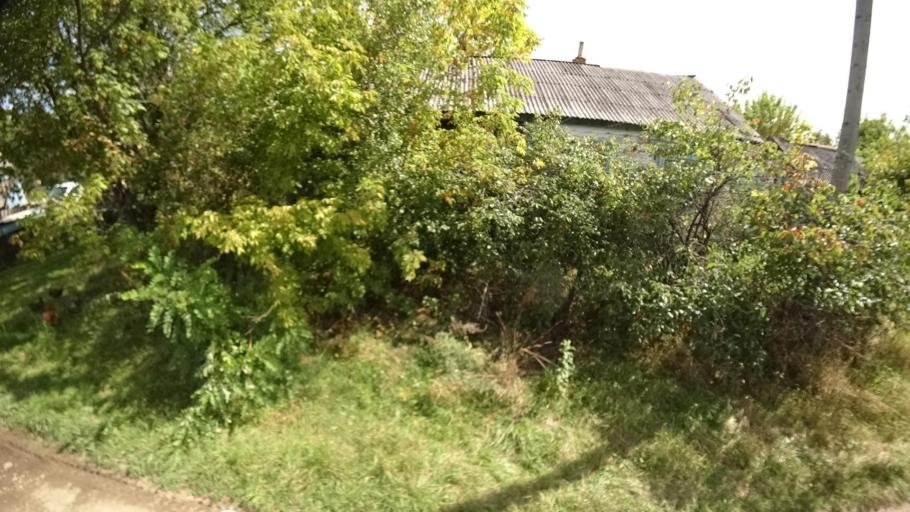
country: RU
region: Primorskiy
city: Yakovlevka
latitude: 44.6445
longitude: 133.5966
